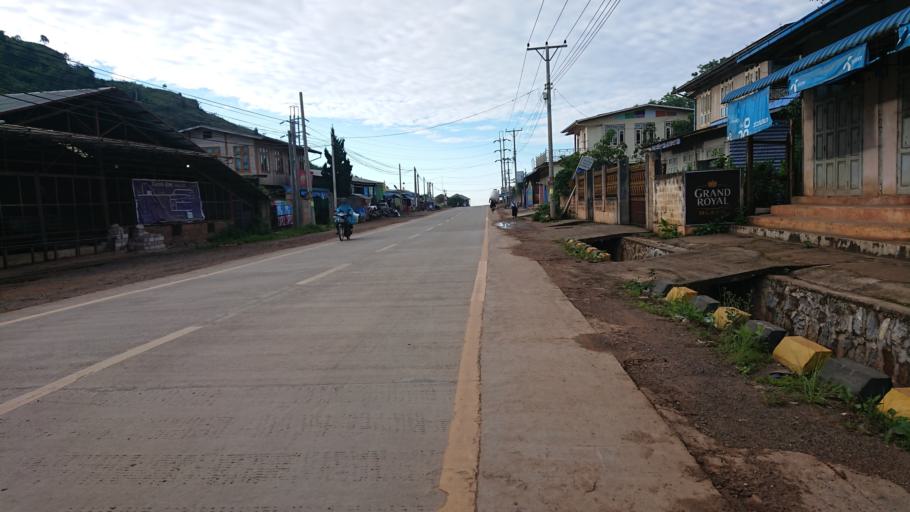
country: MM
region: Shan
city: Taunggyi
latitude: 20.7457
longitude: 97.0505
